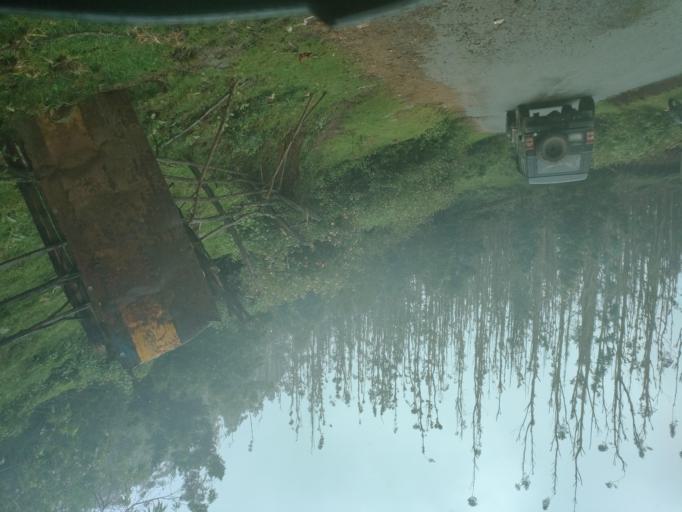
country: IN
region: Tamil Nadu
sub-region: Dindigul
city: Kodaikanal
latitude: 10.2325
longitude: 77.3499
